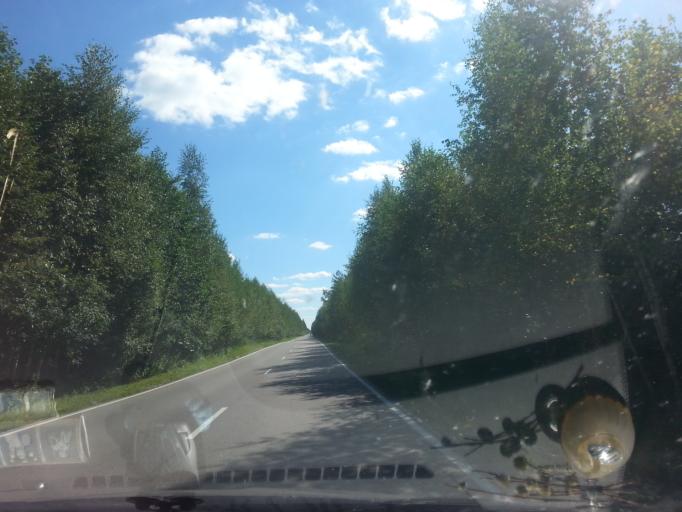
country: RU
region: Vladimir
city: Galitsy
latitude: 56.1306
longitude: 42.8739
